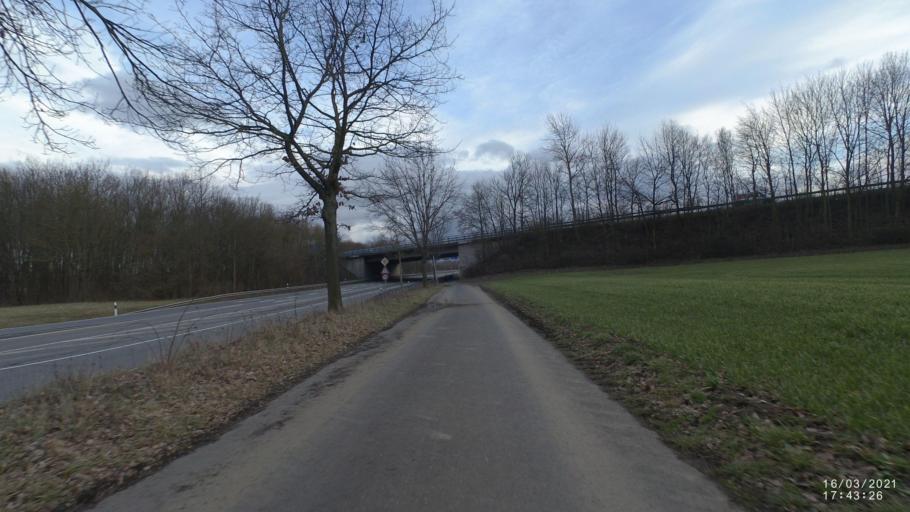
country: DE
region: Rheinland-Pfalz
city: Mendig
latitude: 50.3868
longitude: 7.2692
